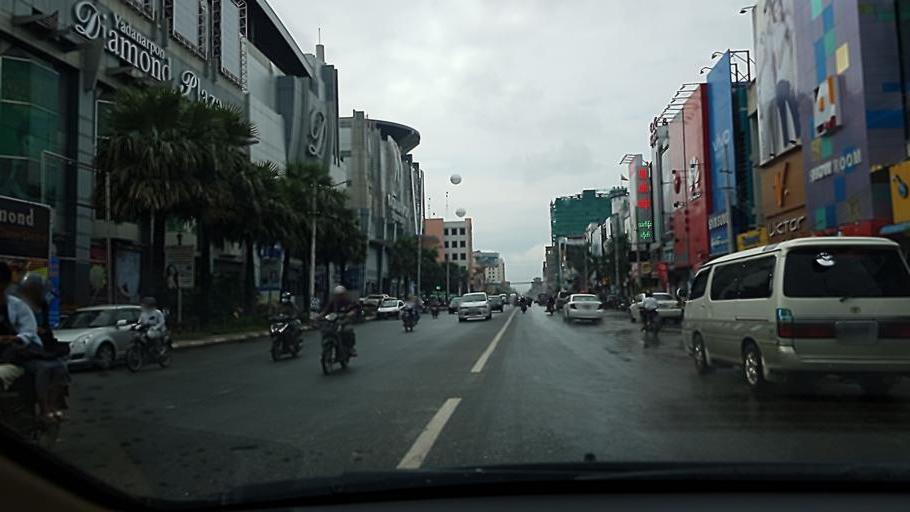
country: MM
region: Mandalay
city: Mandalay
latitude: 21.9723
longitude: 96.0866
